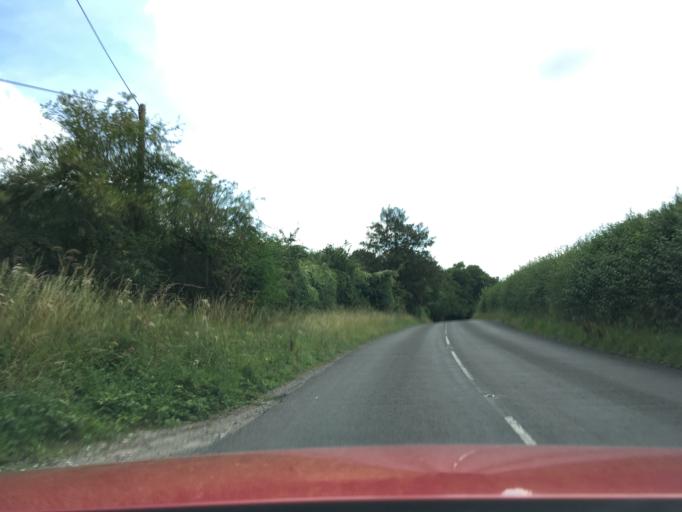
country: GB
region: England
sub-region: Hampshire
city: Kingsclere
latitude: 51.3099
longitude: -1.2551
